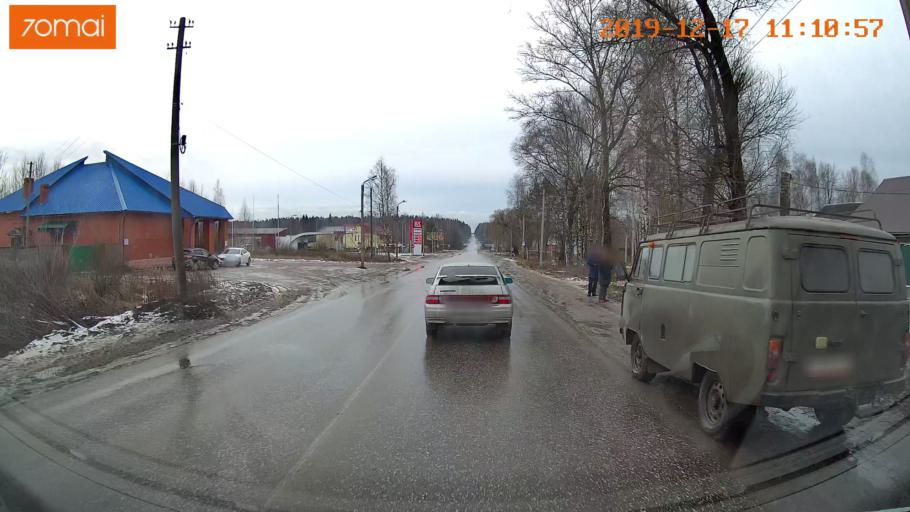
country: RU
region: Vladimir
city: Gus'-Khrustal'nyy
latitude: 55.5895
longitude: 40.6390
